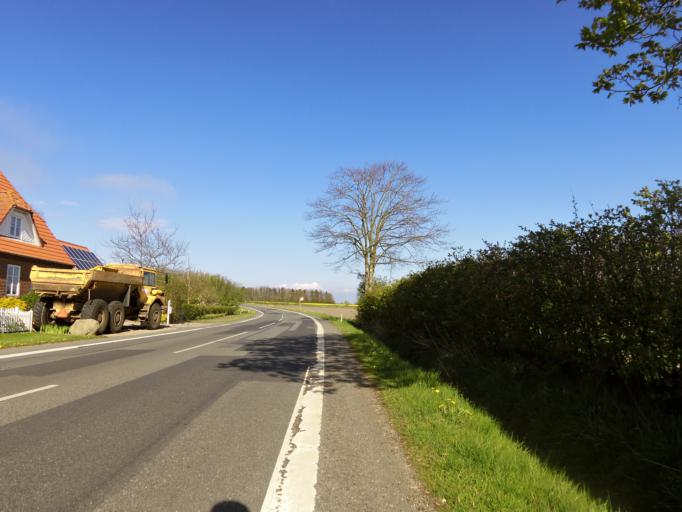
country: DK
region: South Denmark
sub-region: Tonder Kommune
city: Sherrebek
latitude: 55.1548
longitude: 8.8059
